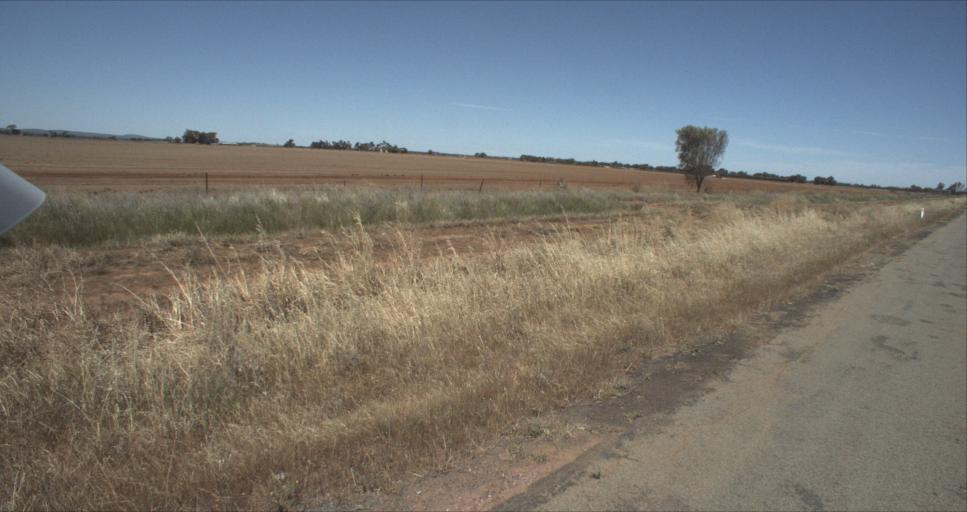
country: AU
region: New South Wales
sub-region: Leeton
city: Leeton
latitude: -34.5164
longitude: 146.3453
